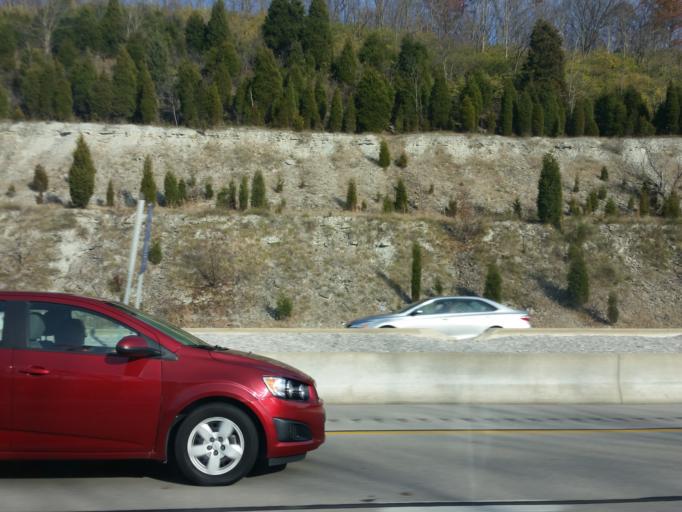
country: US
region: Kentucky
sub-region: Campbell County
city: Wilder
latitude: 39.0528
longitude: -84.4687
